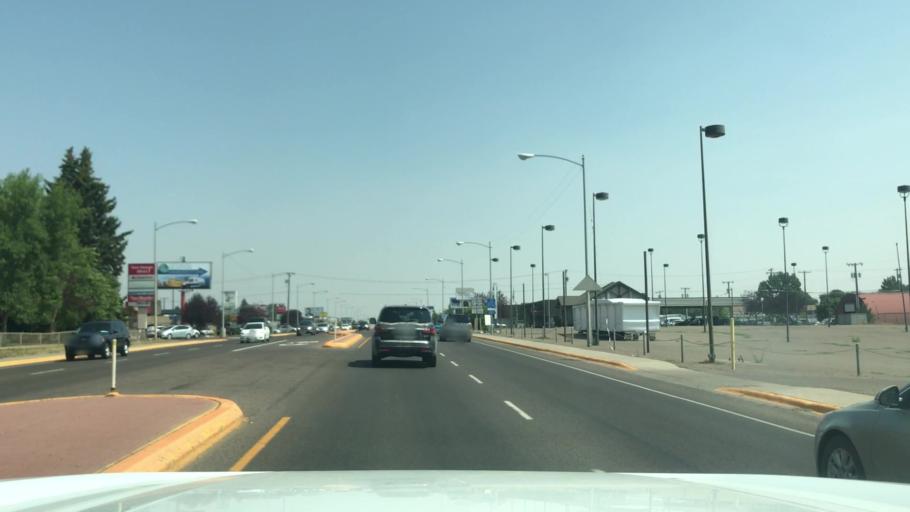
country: US
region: Montana
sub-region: Cascade County
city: Great Falls
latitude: 47.4941
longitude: -111.2595
